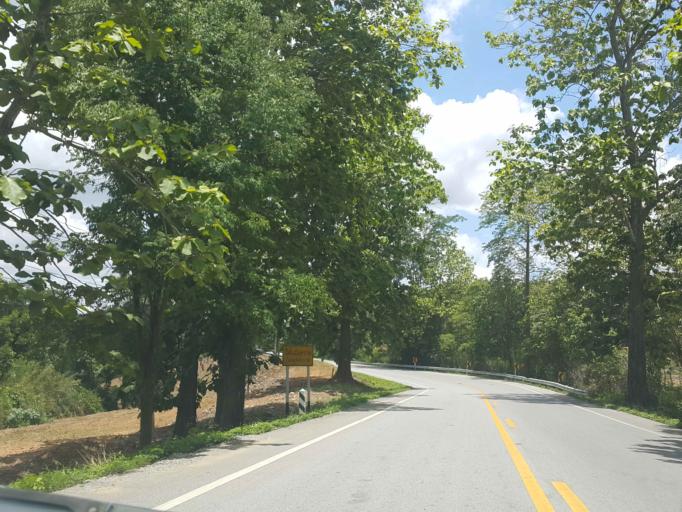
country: TH
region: Nan
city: Wiang Sa
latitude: 18.5260
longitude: 100.6154
